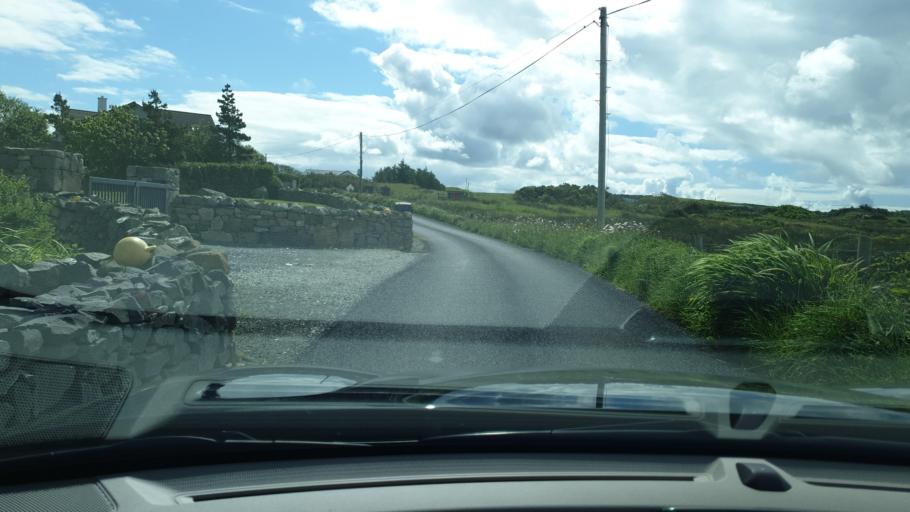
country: IE
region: Connaught
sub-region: County Galway
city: Clifden
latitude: 53.4366
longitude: -10.0763
